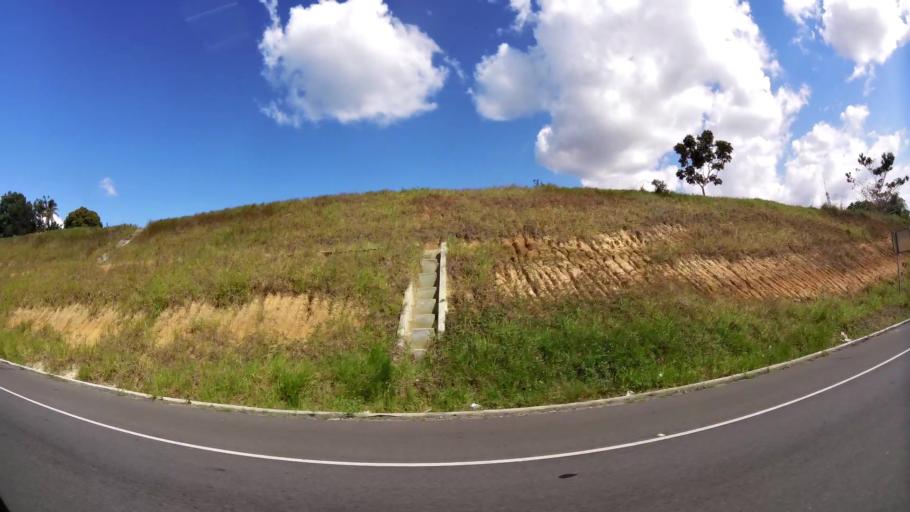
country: DO
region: Santo Domingo
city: Santo Domingo Oeste
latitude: 18.5476
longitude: -70.0785
